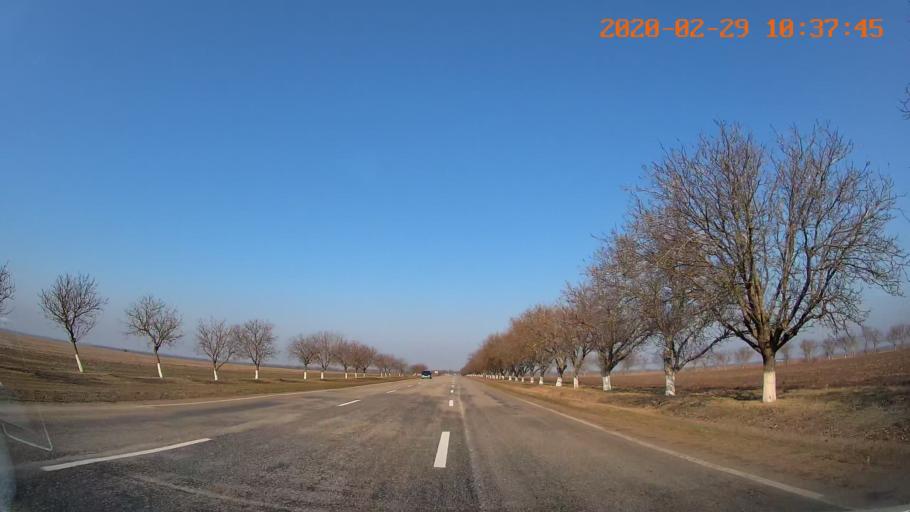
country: MD
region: Anenii Noi
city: Varnita
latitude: 47.0094
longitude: 29.4845
